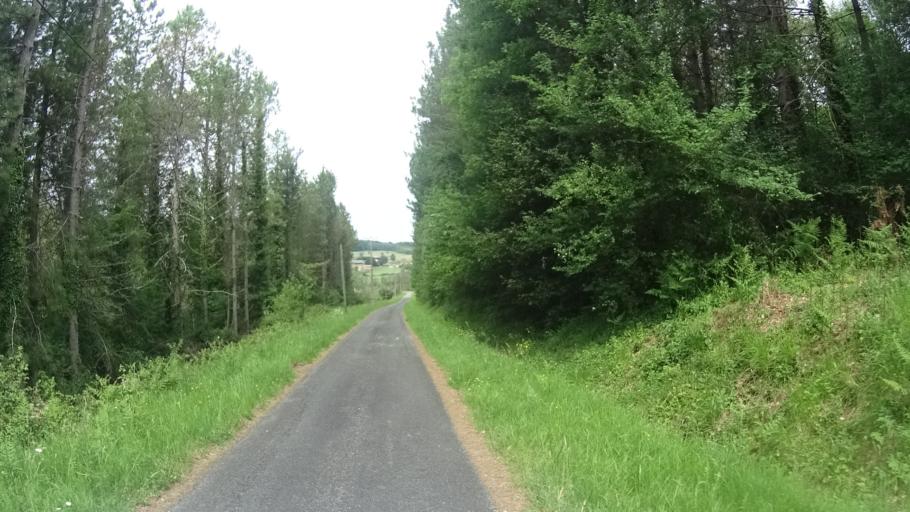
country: FR
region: Aquitaine
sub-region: Departement de la Dordogne
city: Lembras
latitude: 44.9890
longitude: 0.5225
